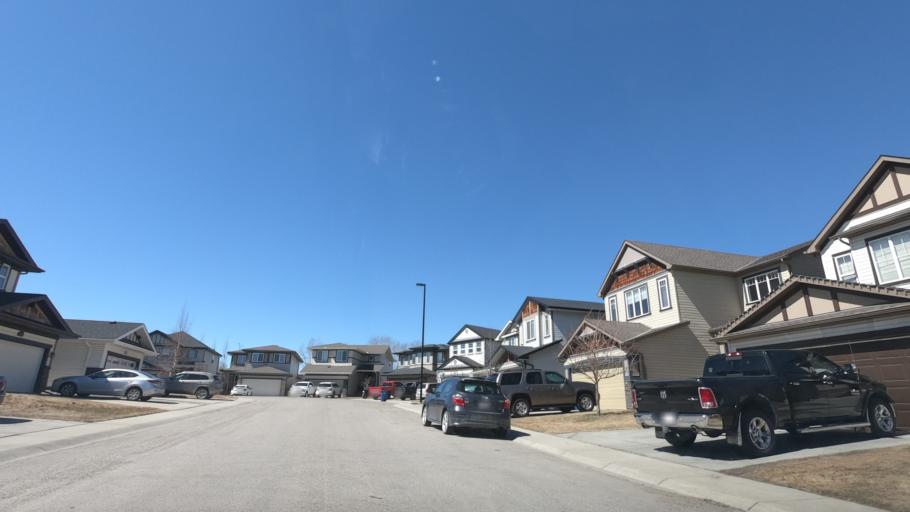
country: CA
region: Alberta
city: Airdrie
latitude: 51.3015
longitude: -114.0470
